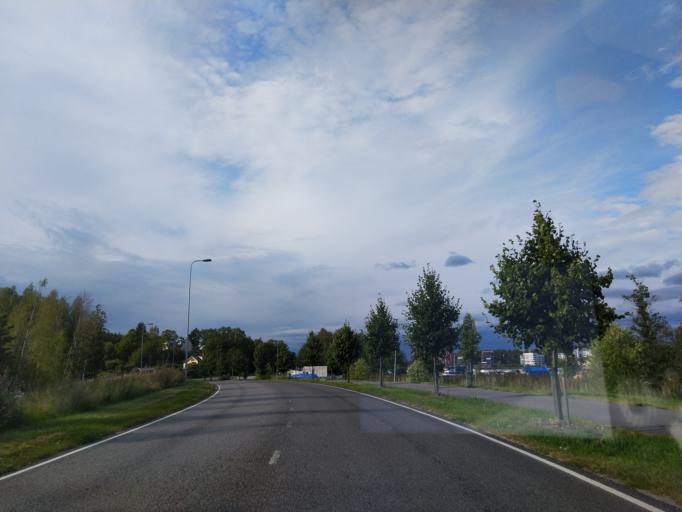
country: FI
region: Varsinais-Suomi
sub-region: Turku
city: Turku
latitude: 60.4225
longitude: 22.2277
